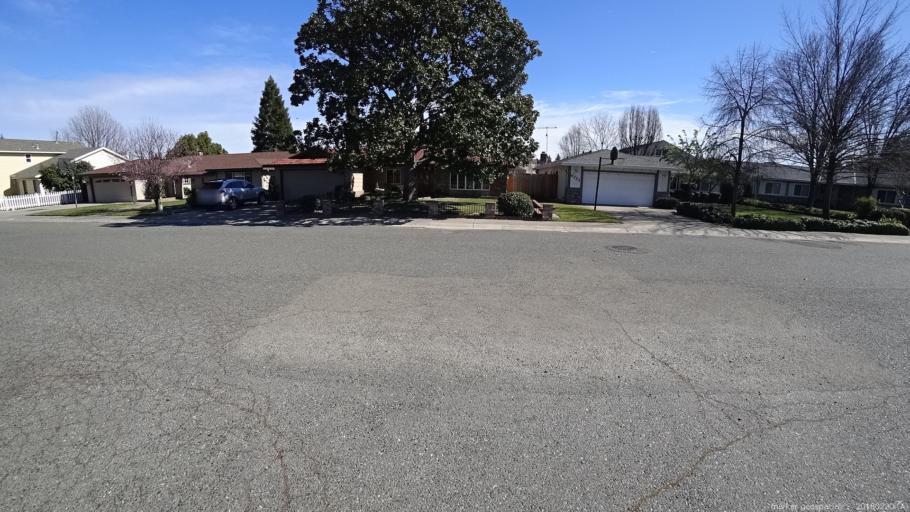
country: US
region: California
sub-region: Sacramento County
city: Orangevale
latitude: 38.6799
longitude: -121.2192
